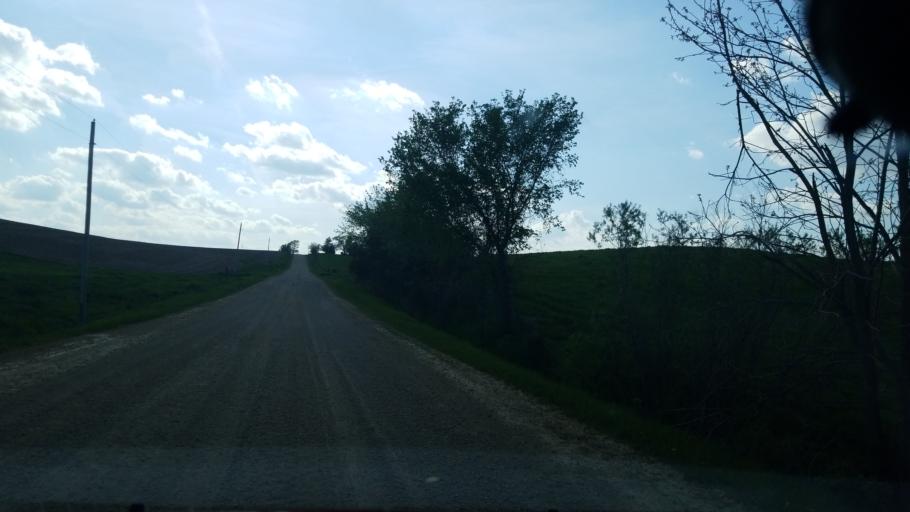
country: US
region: Iowa
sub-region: Jackson County
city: Maquoketa
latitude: 42.2150
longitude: -90.7062
